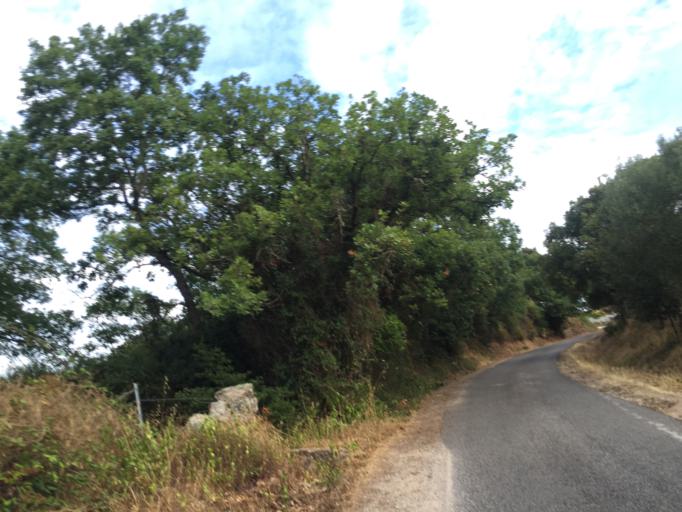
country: IT
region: Sardinia
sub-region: Provincia di Olbia-Tempio
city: Aggius
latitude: 40.9270
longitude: 9.0713
